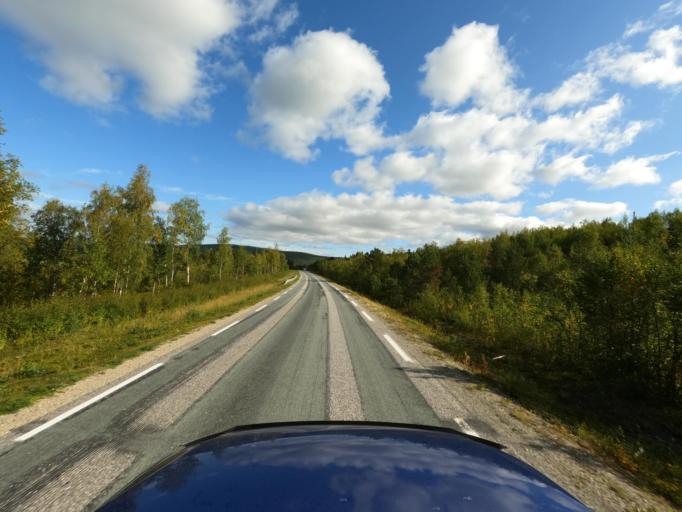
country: NO
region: Finnmark Fylke
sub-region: Karasjok
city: Karasjohka
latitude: 69.4291
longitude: 25.7768
